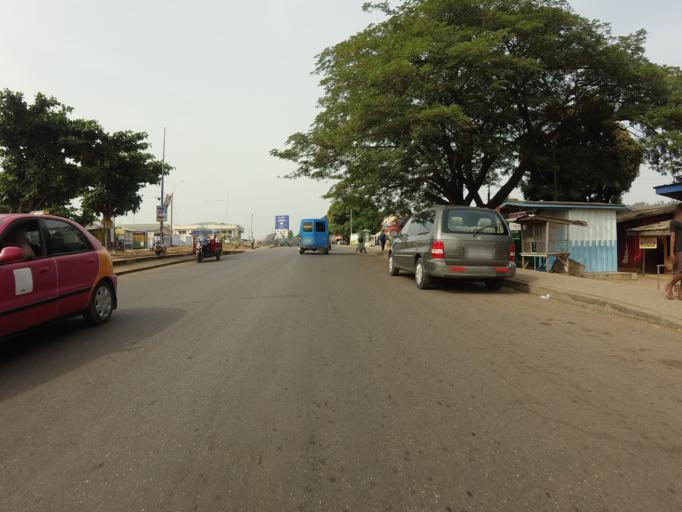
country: GH
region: Volta
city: Ho
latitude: 6.6124
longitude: 0.4632
